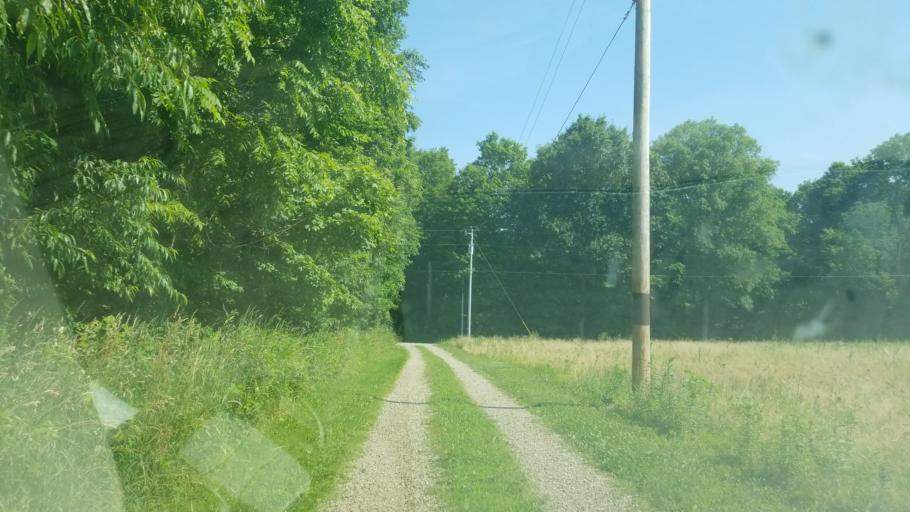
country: US
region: Ohio
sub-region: Sandusky County
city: Bellville
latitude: 40.6084
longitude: -82.5589
